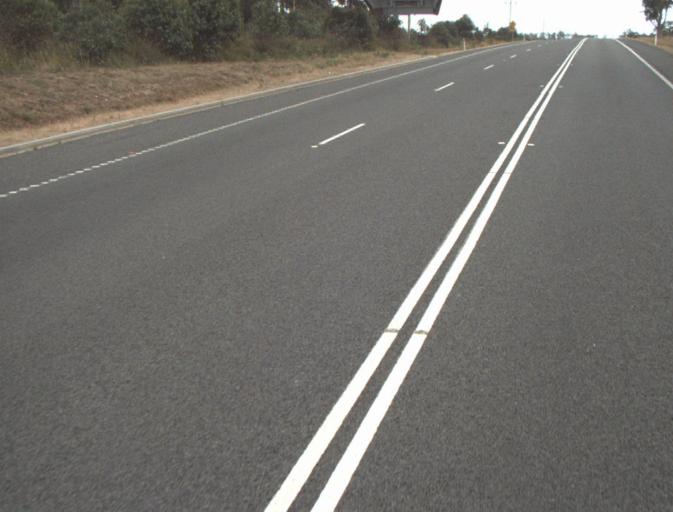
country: AU
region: Tasmania
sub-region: Launceston
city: Mayfield
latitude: -41.2584
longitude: 147.0260
